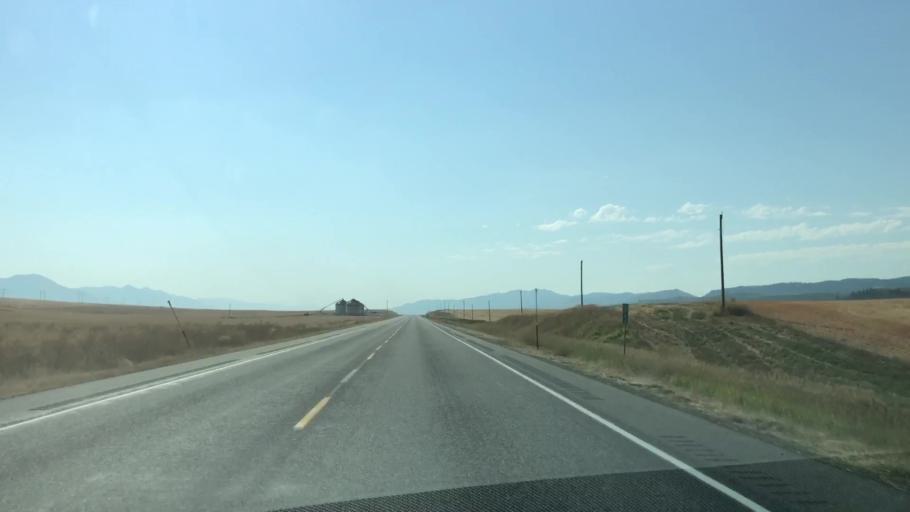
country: US
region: Idaho
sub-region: Teton County
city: Victor
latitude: 43.5196
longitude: -111.4901
